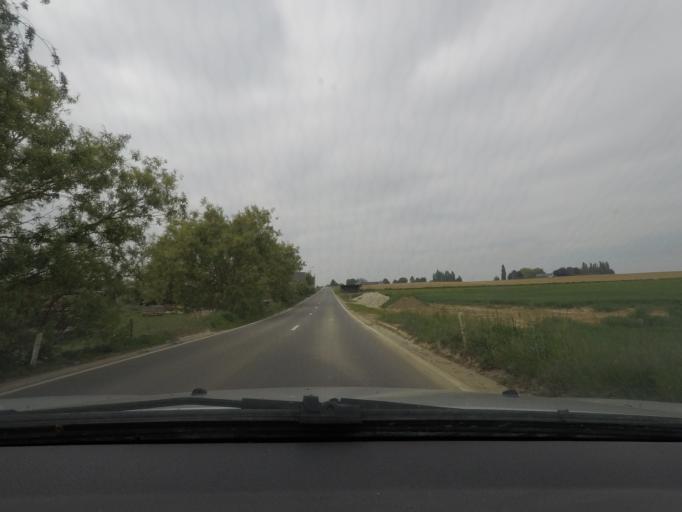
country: BE
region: Wallonia
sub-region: Province de Namur
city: Noville-les-Bois
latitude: 50.5066
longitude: 5.0016
